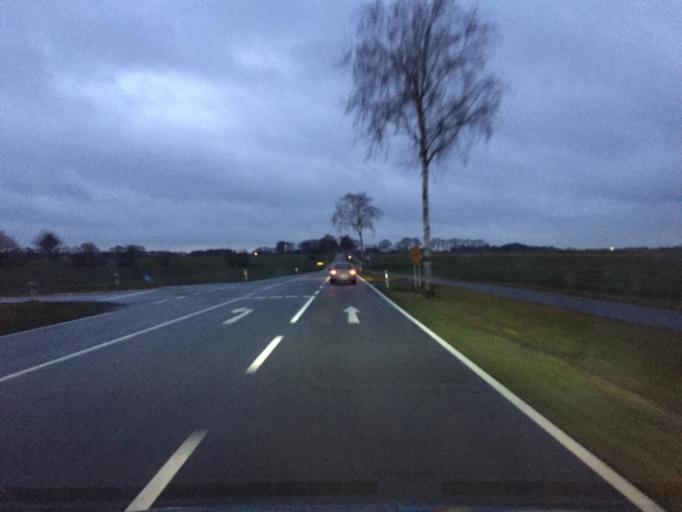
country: DE
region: Lower Saxony
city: Sulingen
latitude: 52.7021
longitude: 8.8073
